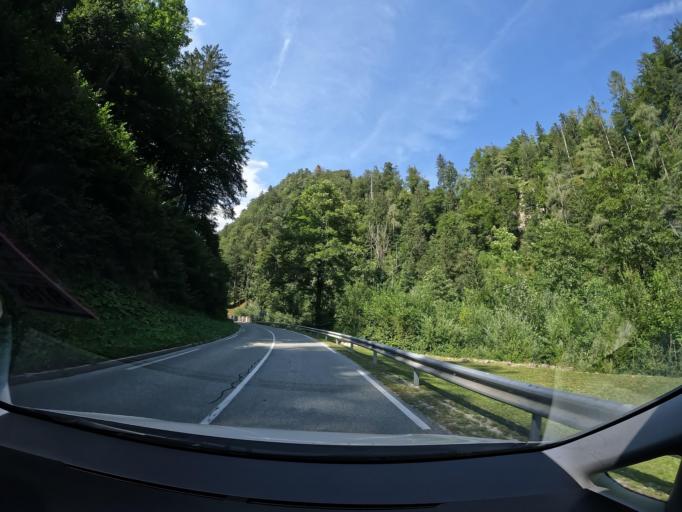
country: SI
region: Trzic
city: Trzic
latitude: 46.3894
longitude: 14.3567
